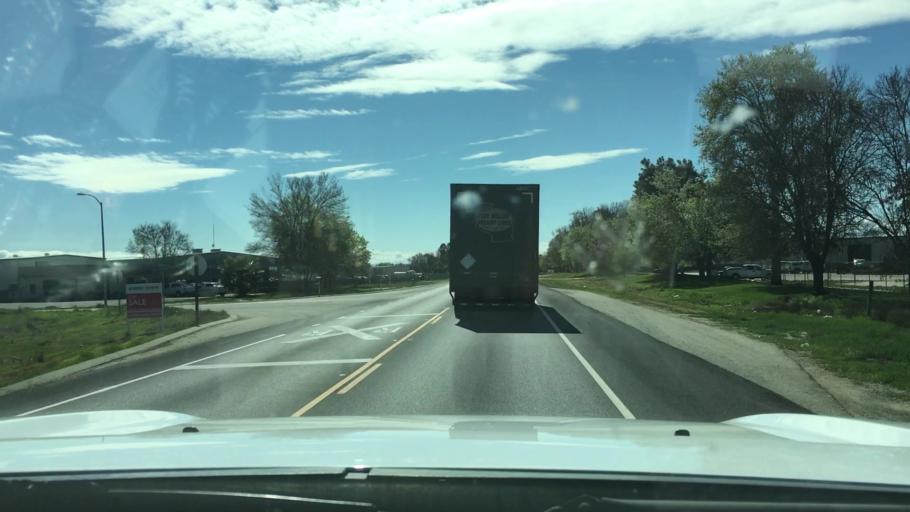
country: US
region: California
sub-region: Kern County
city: Shafter
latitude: 35.4490
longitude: -119.2552
